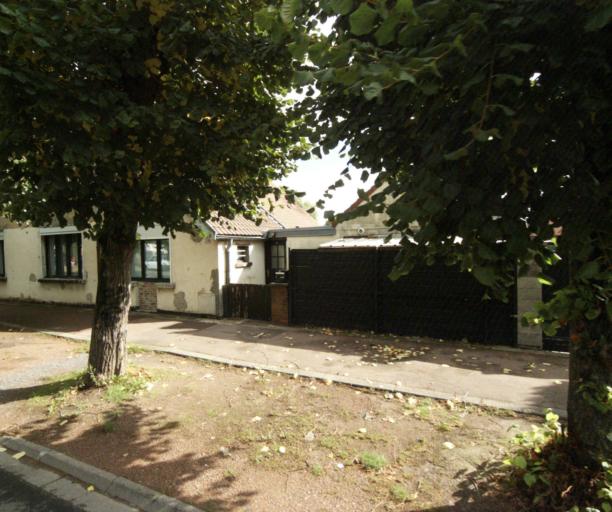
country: FR
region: Nord-Pas-de-Calais
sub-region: Departement du Nord
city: Lomme
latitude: 50.6407
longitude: 2.9904
